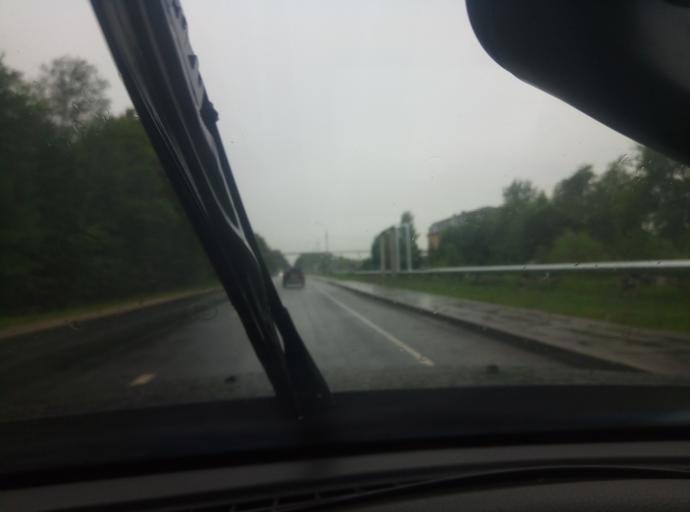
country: RU
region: Moskovskaya
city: Protvino
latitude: 54.8842
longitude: 37.2035
